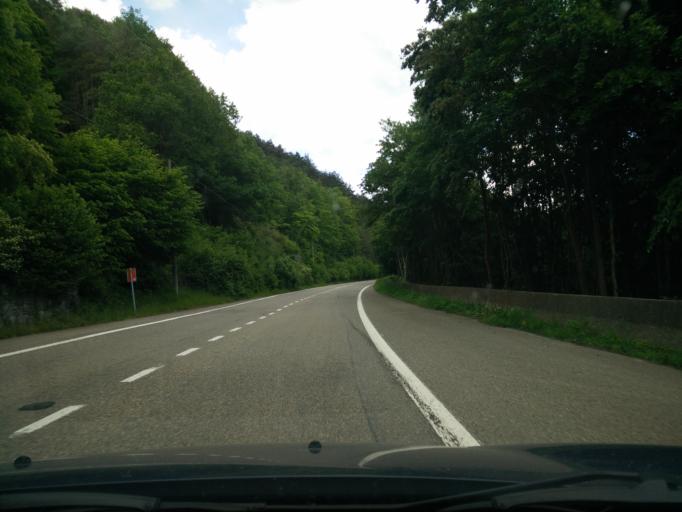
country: FR
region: Champagne-Ardenne
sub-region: Departement des Ardennes
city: Vireux-Molhain
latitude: 50.0772
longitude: 4.6107
